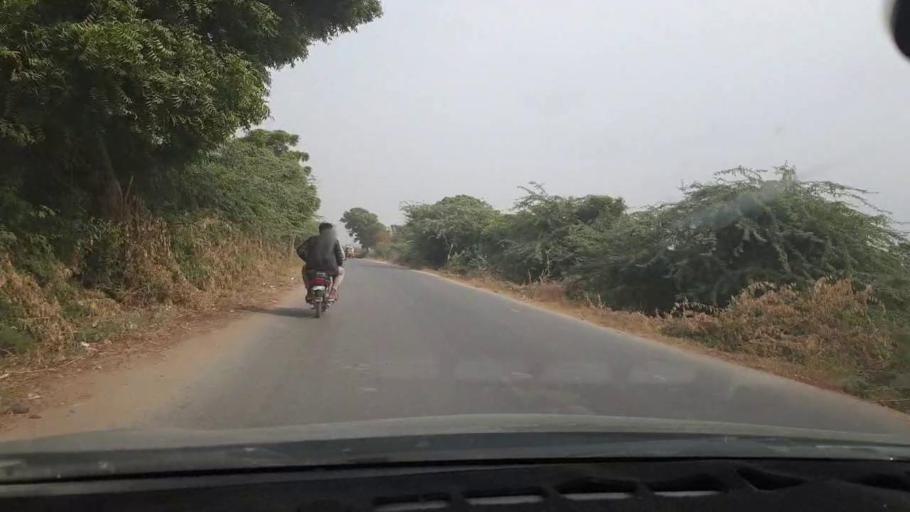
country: PK
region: Sindh
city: Malir Cantonment
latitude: 24.9138
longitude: 67.2632
